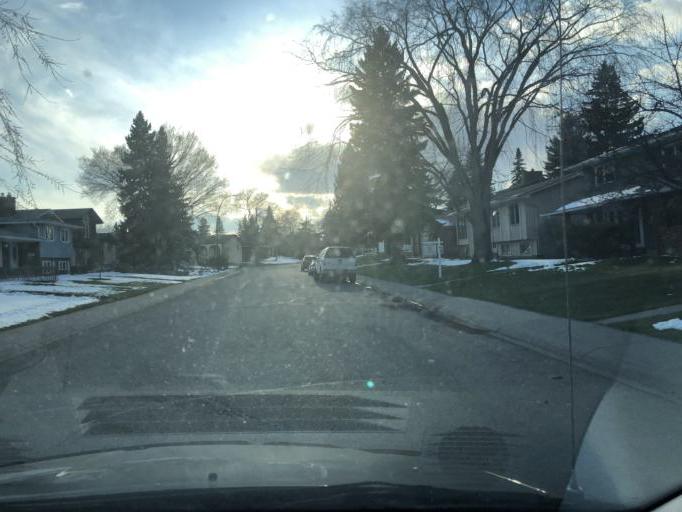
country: CA
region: Alberta
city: Calgary
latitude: 50.9419
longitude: -114.0381
